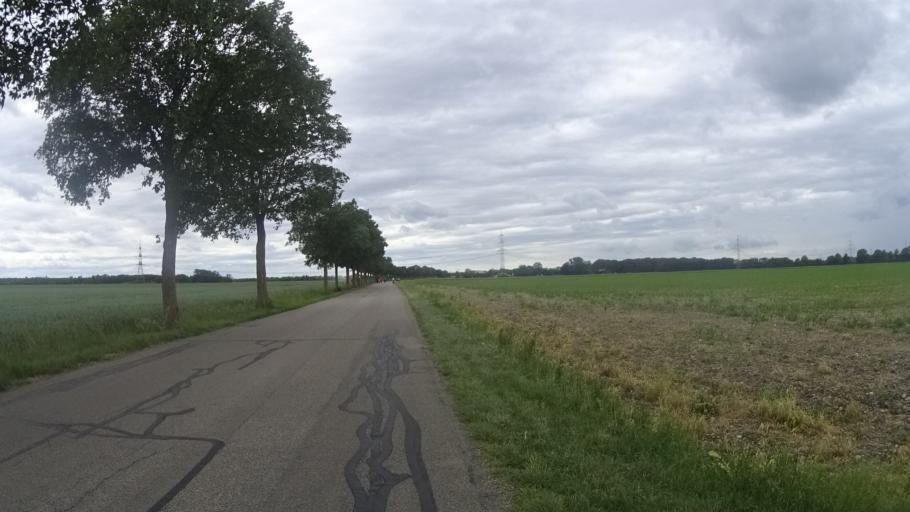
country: DE
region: Bavaria
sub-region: Upper Bavaria
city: Eching
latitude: 48.2941
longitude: 11.6059
